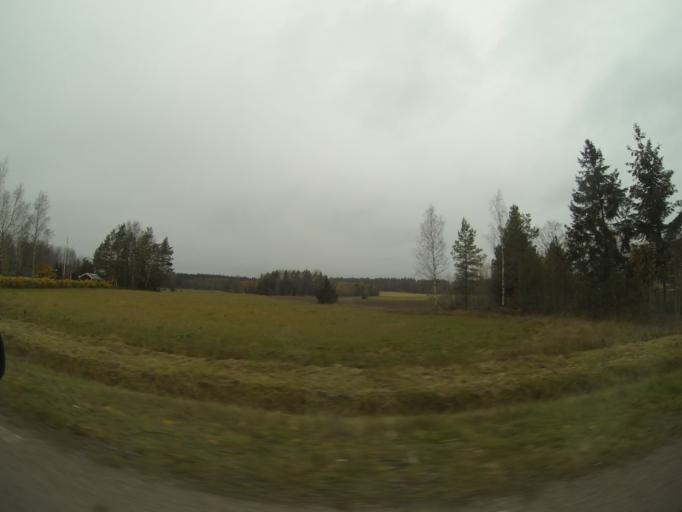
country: SE
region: Vaestmanland
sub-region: Kopings Kommun
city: Koping
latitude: 59.5841
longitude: 16.0845
